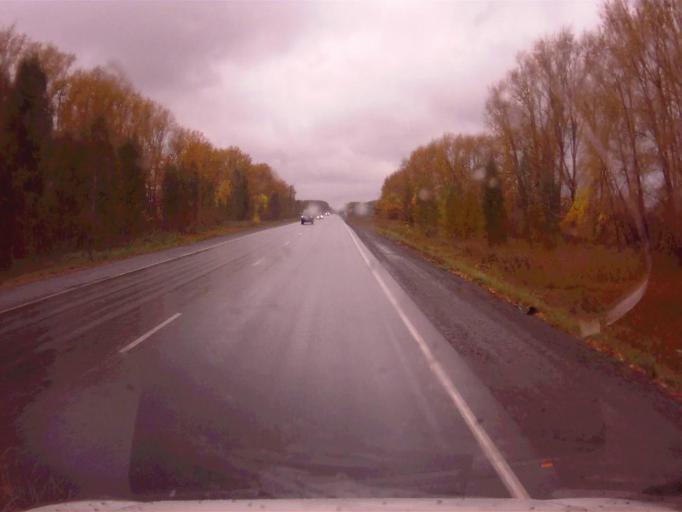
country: RU
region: Chelyabinsk
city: Argayash
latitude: 55.4523
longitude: 60.9341
